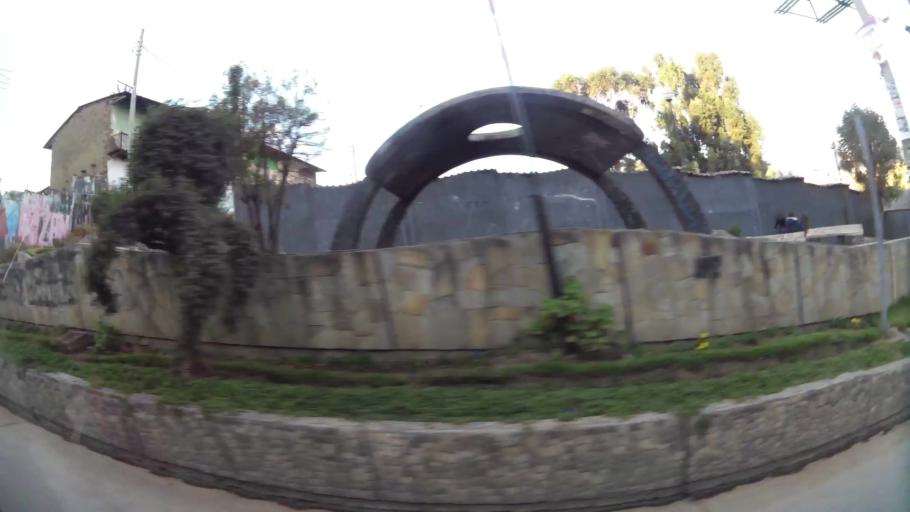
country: PE
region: Junin
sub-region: Provincia de Huancayo
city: El Tambo
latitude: -12.0645
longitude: -75.2128
